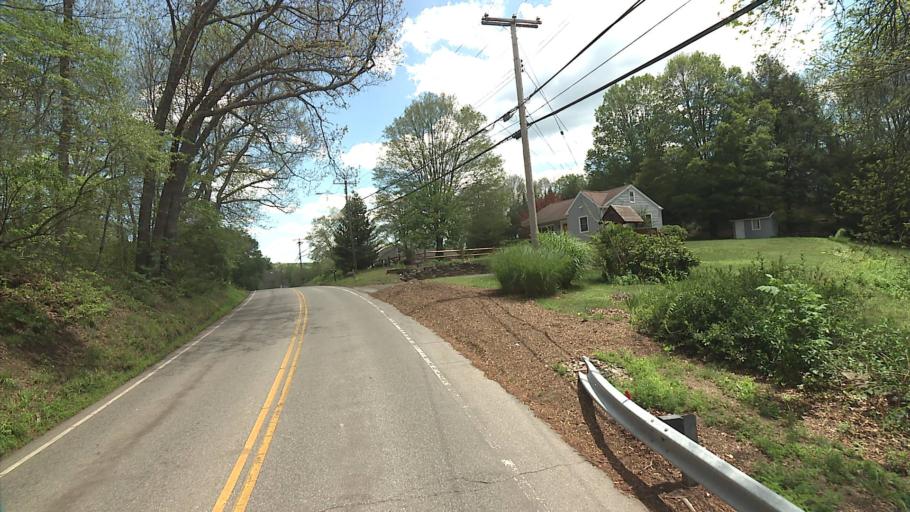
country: US
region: Connecticut
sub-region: Middlesex County
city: Moodus
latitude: 41.5006
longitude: -72.4626
